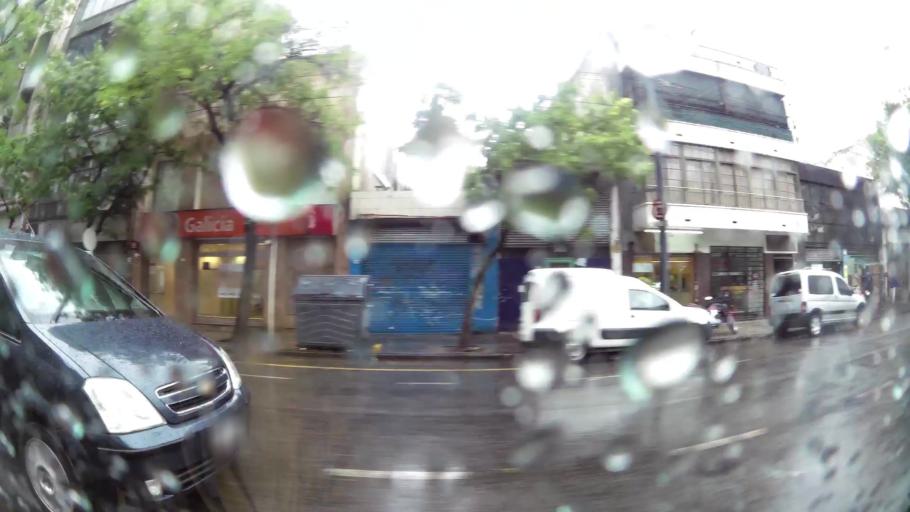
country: AR
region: Buenos Aires F.D.
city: Buenos Aires
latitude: -34.6221
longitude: -58.3916
